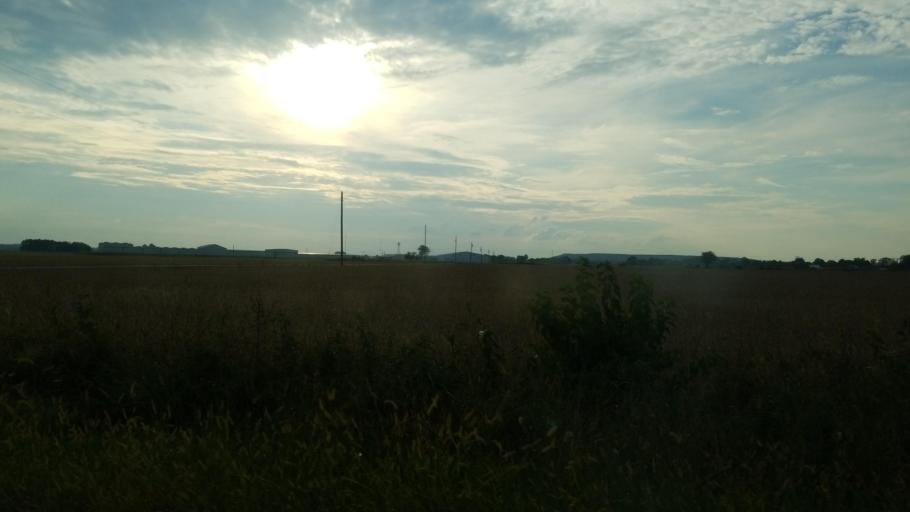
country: US
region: Illinois
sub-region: Saline County
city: Harrisburg
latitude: 37.8126
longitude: -88.5397
